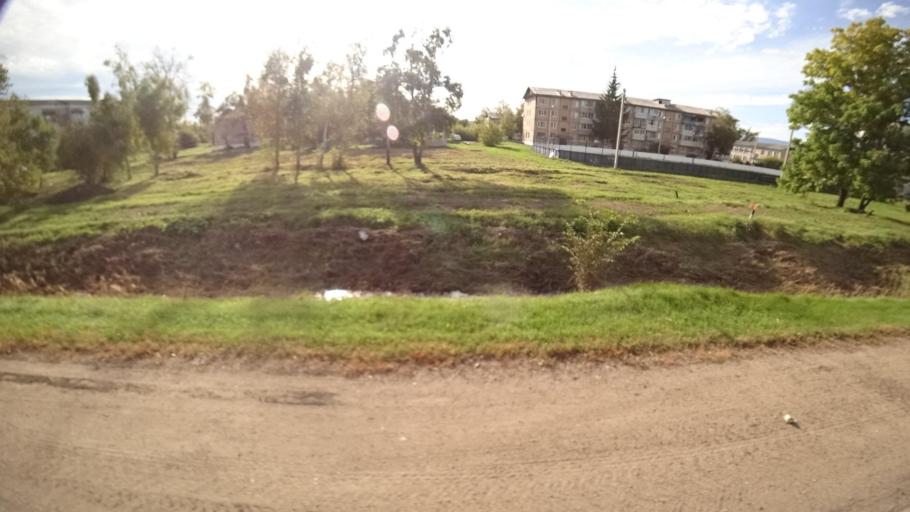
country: RU
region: Primorskiy
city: Dostoyevka
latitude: 44.2903
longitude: 133.4264
